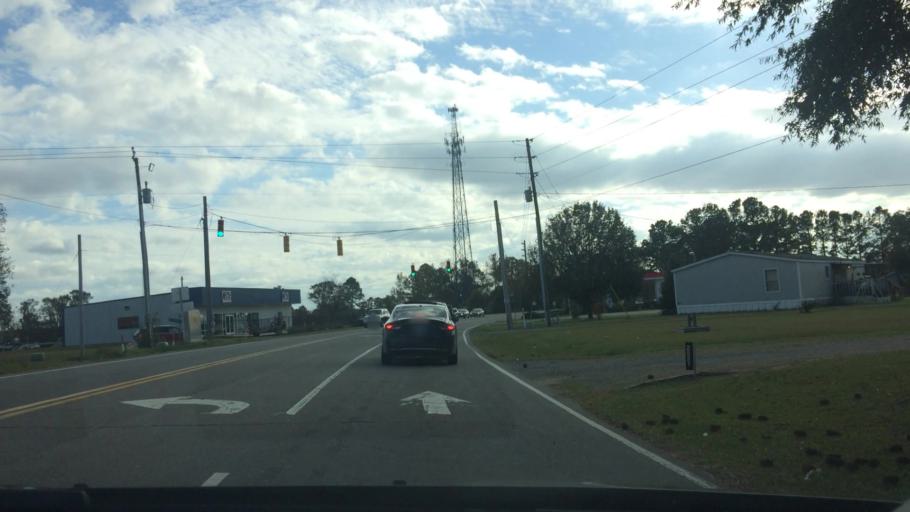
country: US
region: North Carolina
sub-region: Wayne County
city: Elroy
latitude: 35.4053
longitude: -77.8978
